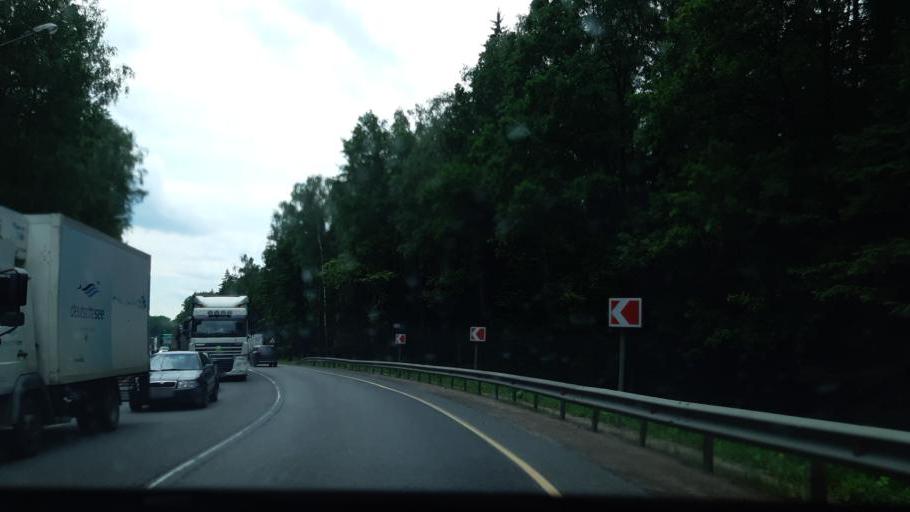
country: RU
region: Moskovskaya
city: Dorokhovo
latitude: 55.5234
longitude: 36.3533
